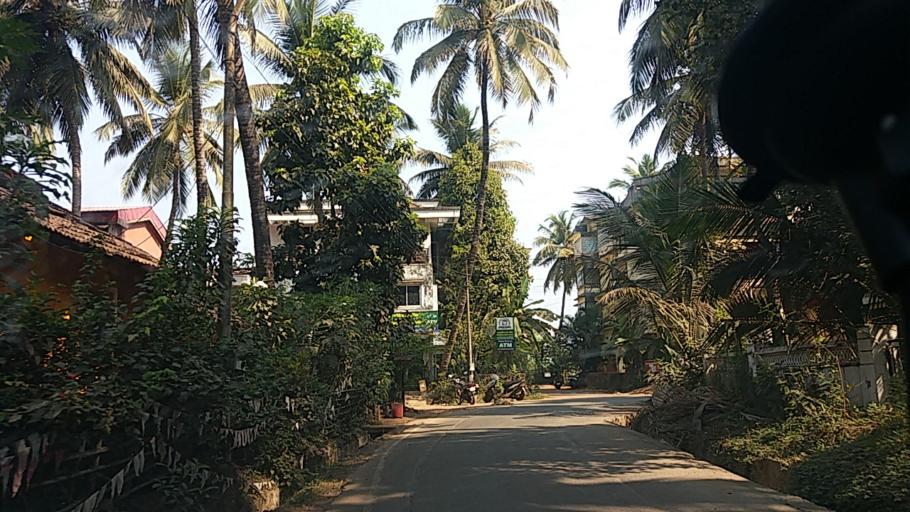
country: IN
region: Goa
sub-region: South Goa
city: Madgaon
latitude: 15.2882
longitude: 73.9528
